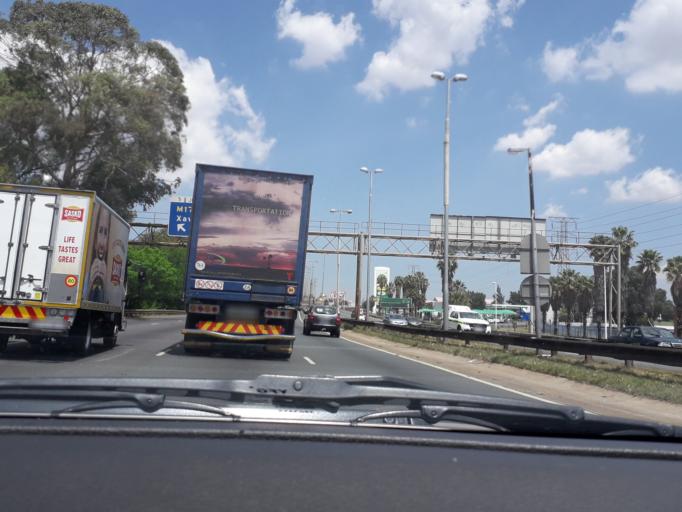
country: ZA
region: Gauteng
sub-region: City of Johannesburg Metropolitan Municipality
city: Johannesburg
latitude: -26.2409
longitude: 28.0128
